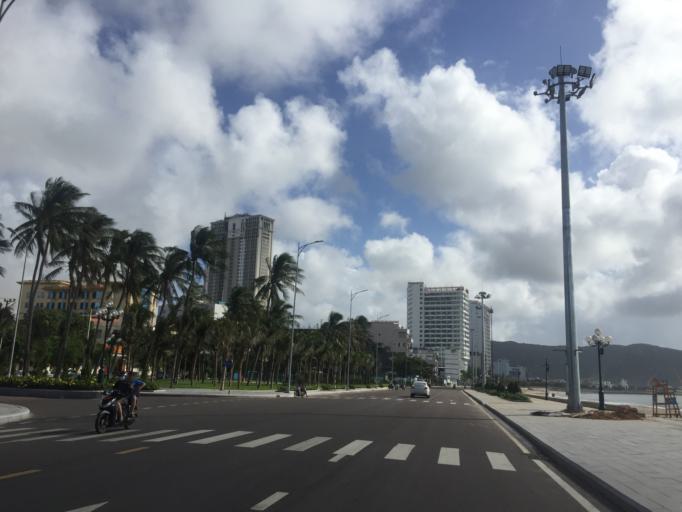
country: VN
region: Binh Dinh
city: Qui Nhon
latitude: 13.7709
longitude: 109.2374
